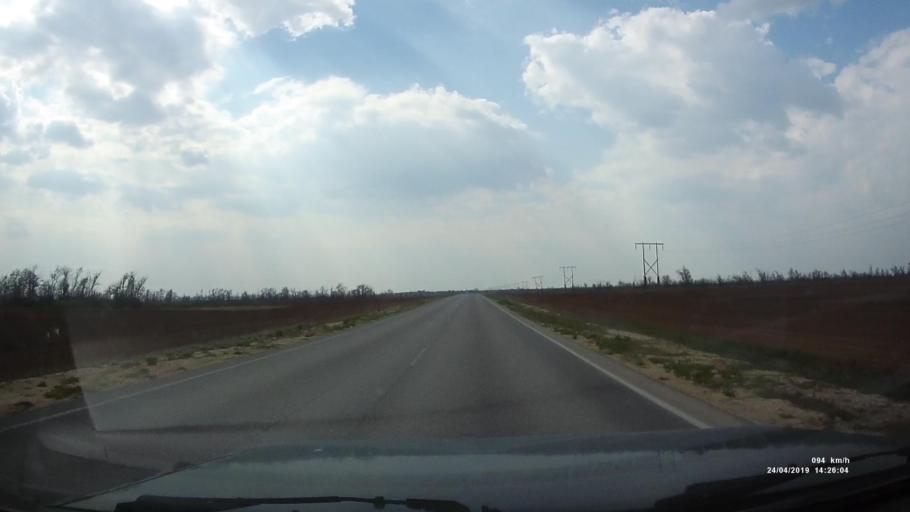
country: RU
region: Kalmykiya
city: Arshan'
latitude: 46.3326
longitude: 44.0698
